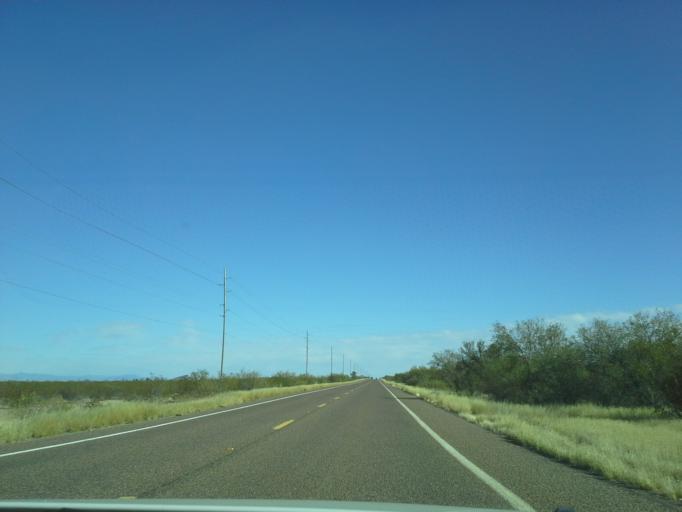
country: US
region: Arizona
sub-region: Yavapai County
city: Congress
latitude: 33.9429
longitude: -113.0358
